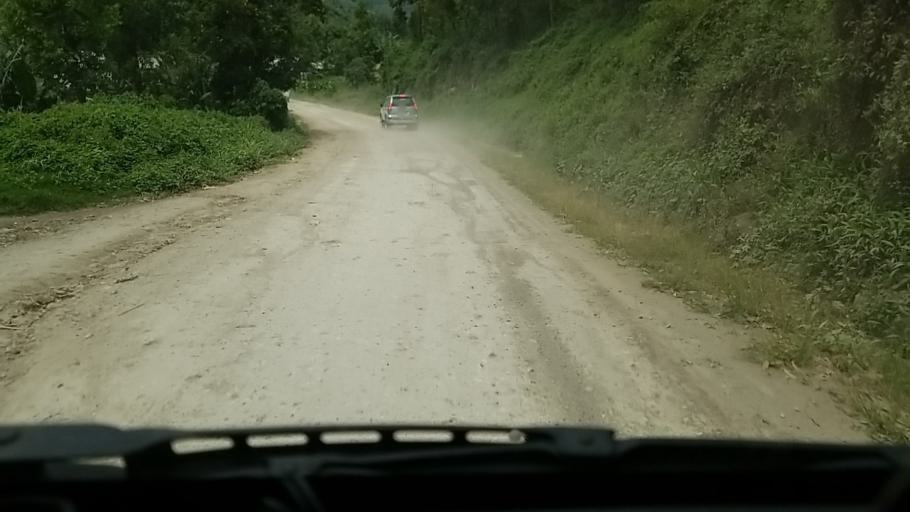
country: CD
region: Nord Kivu
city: Sake
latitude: -1.5907
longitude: 29.0412
